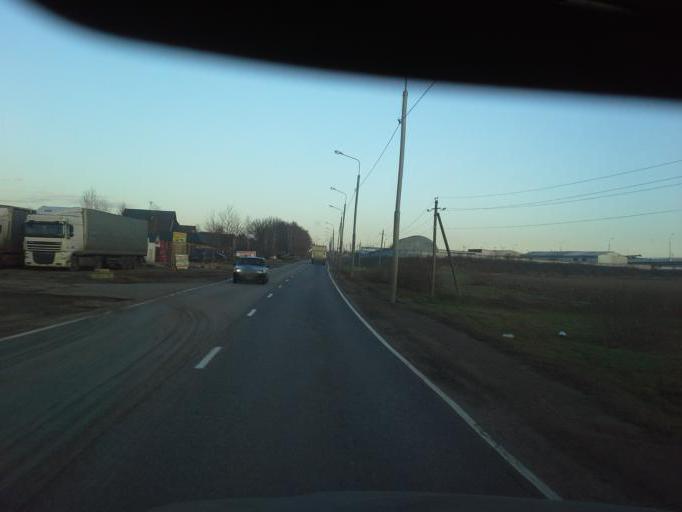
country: RU
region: Moscow
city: Vnukovo
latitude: 55.5877
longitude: 37.2065
